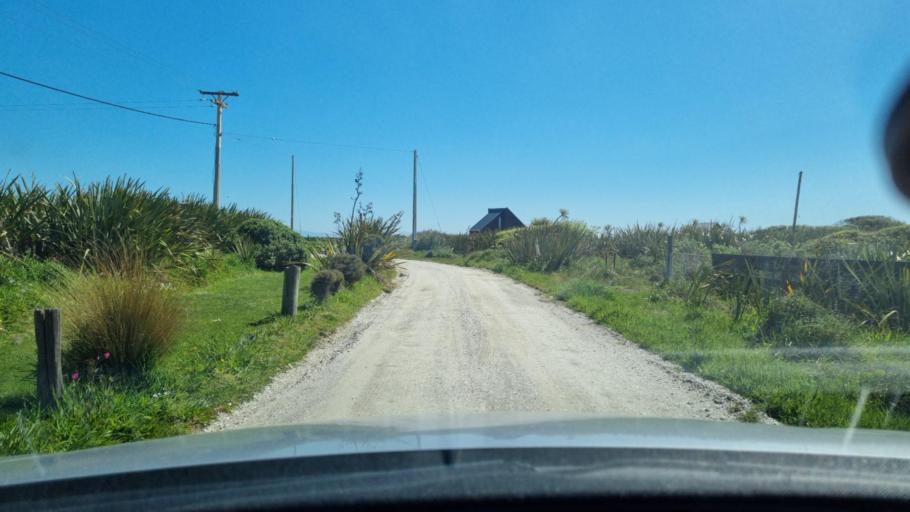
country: NZ
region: Southland
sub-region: Invercargill City
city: Invercargill
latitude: -46.4296
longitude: 168.2318
